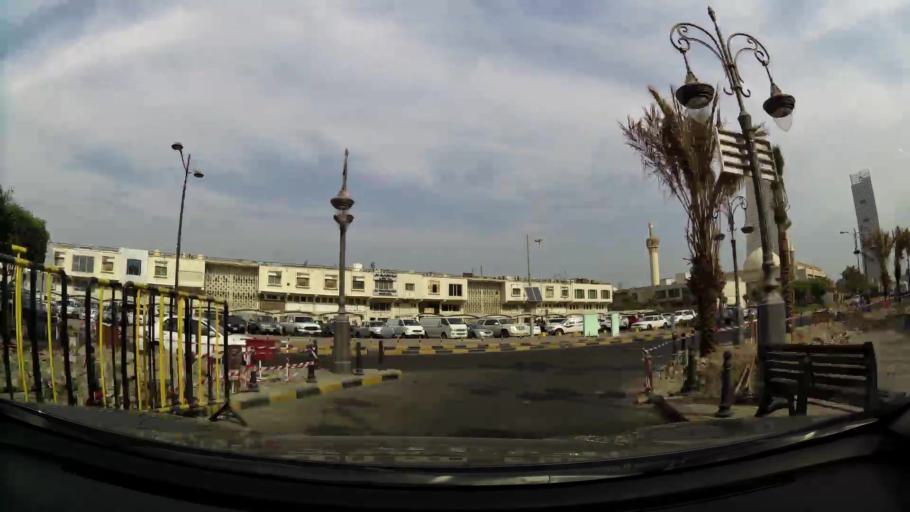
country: KW
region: Al Asimah
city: Kuwait City
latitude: 29.3768
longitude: 47.9733
